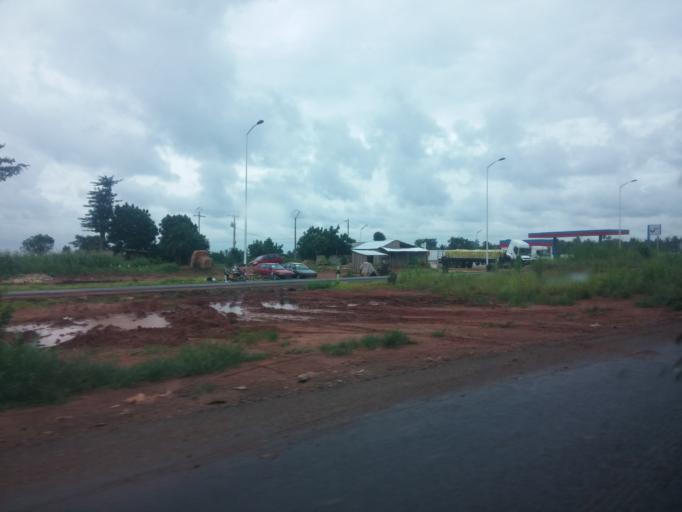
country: TG
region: Maritime
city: Tsevie
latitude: 6.3505
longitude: 1.2124
